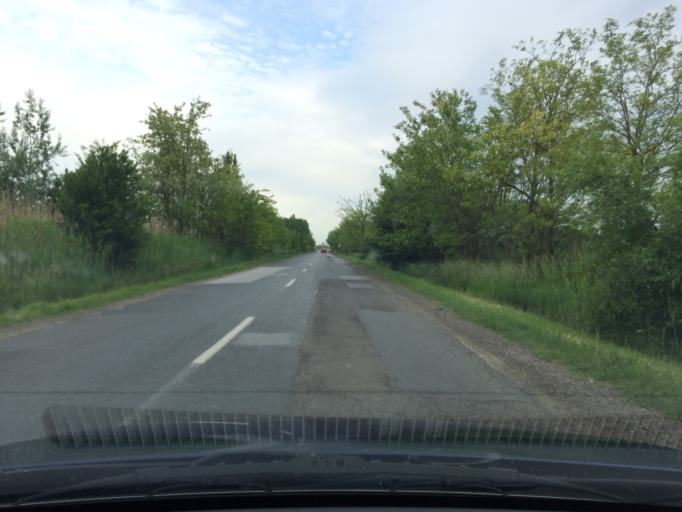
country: HU
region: Hajdu-Bihar
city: Hajdunanas
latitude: 47.8898
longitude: 21.4123
